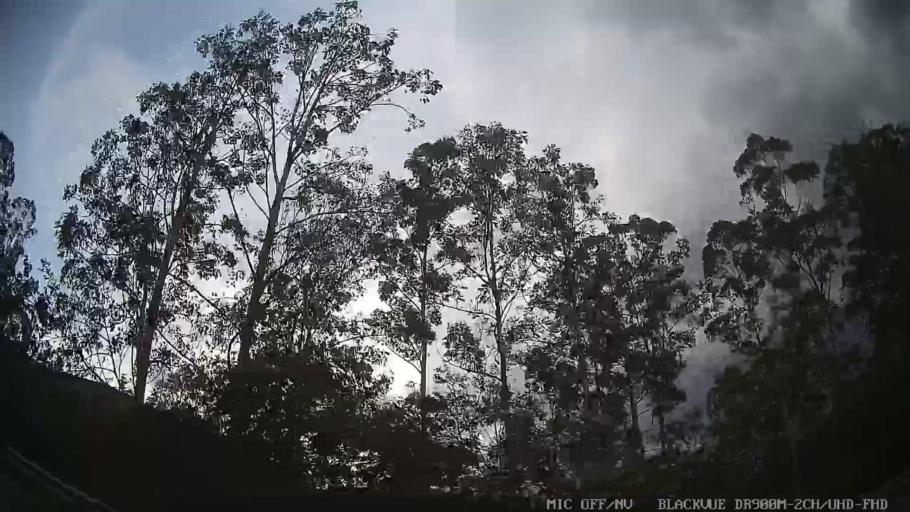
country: BR
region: Sao Paulo
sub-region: Itatiba
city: Itatiba
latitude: -22.9497
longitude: -46.8174
